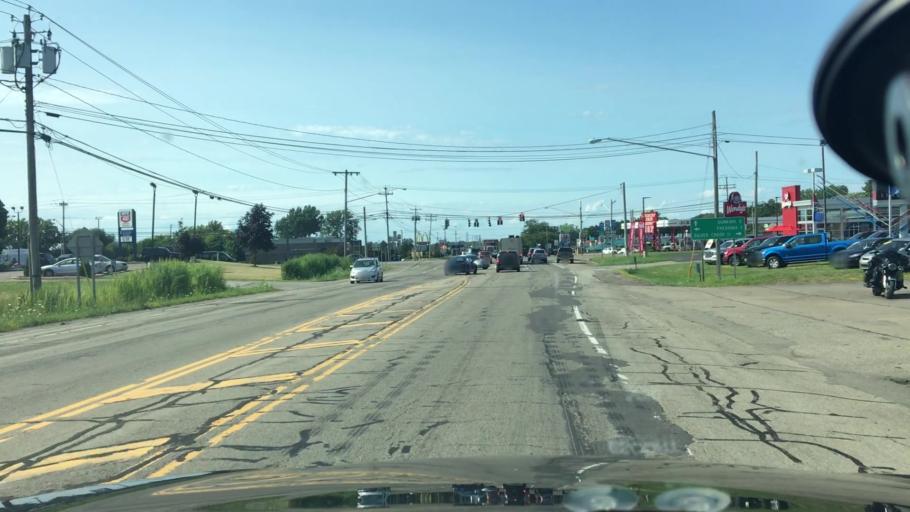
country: US
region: New York
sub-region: Chautauqua County
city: Fredonia
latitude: 42.4494
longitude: -79.3073
